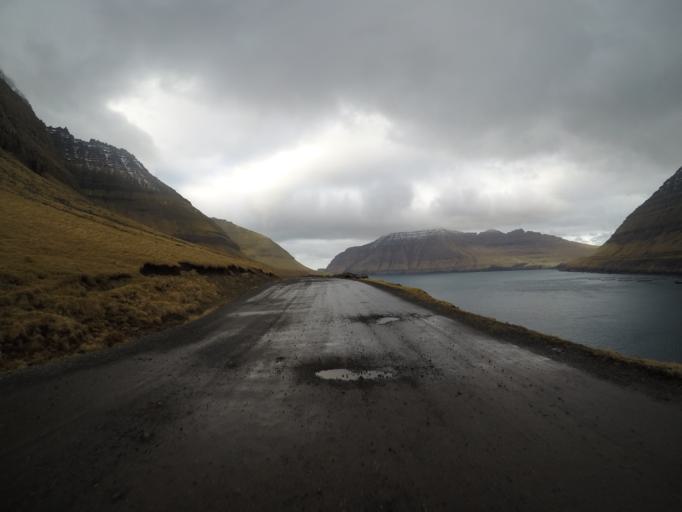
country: FO
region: Nordoyar
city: Klaksvik
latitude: 62.3367
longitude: -6.5786
